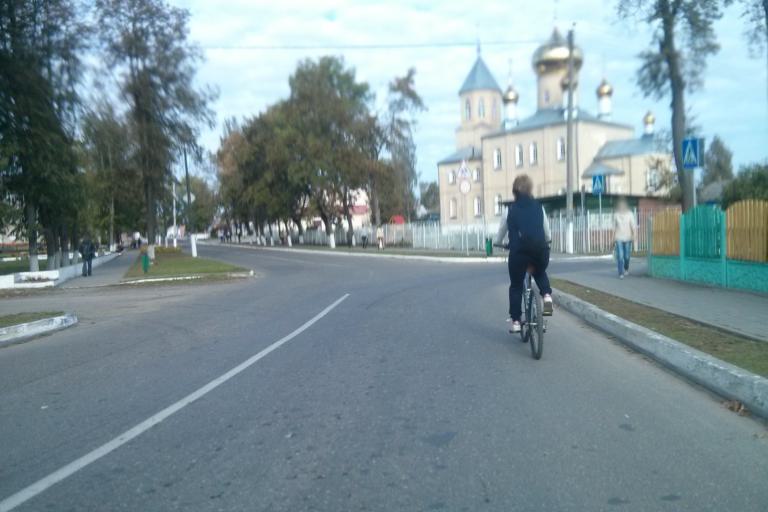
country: BY
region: Minsk
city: Chervyen'
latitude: 53.7117
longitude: 28.4247
